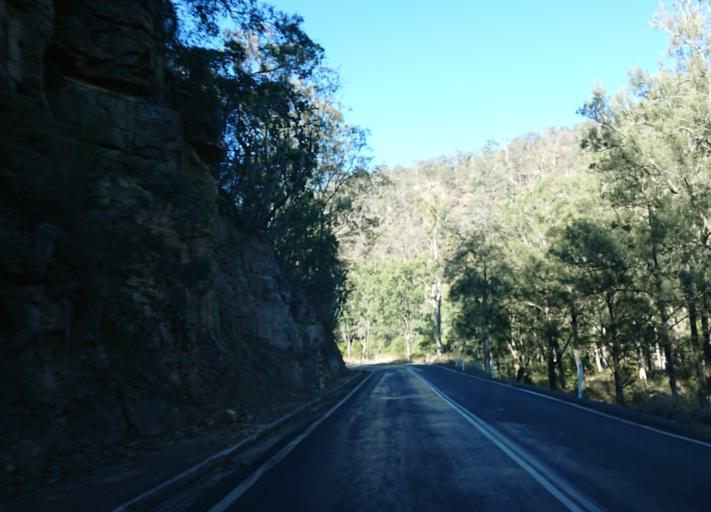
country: AU
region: Queensland
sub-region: Toowoomba
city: Top Camp
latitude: -27.7462
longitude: 152.0912
